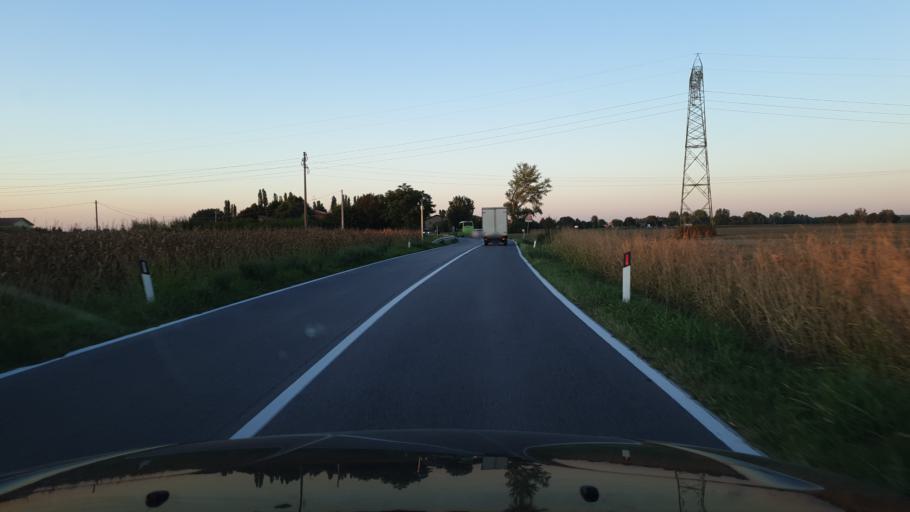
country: IT
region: Emilia-Romagna
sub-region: Provincia di Bologna
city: Progresso
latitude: 44.5695
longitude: 11.4038
